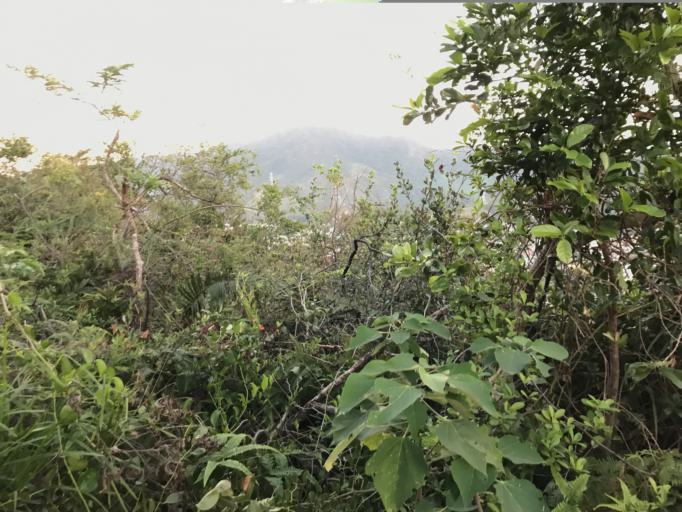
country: HK
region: Tai Po
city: Tai Po
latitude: 22.4704
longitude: 114.1462
